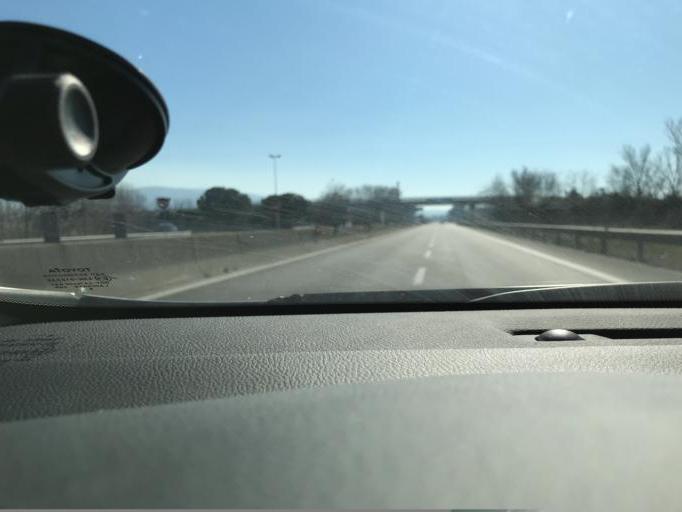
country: IT
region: Umbria
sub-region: Provincia di Perugia
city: San Martino in Campo
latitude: 43.0347
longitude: 12.4113
